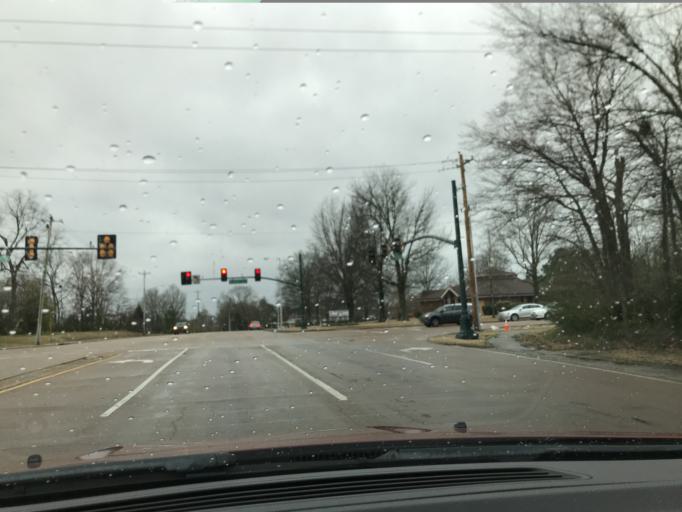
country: US
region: Tennessee
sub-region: Shelby County
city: Collierville
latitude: 35.0543
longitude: -89.6862
